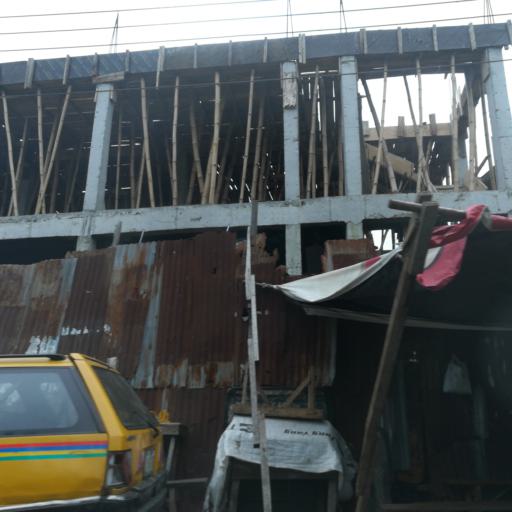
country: NG
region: Lagos
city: Ebute Metta
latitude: 6.4821
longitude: 3.3875
